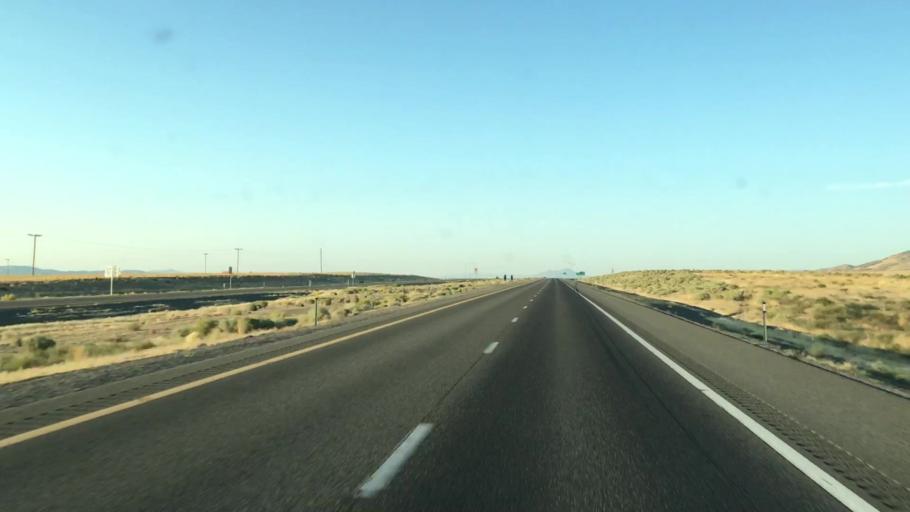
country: US
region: Nevada
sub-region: Humboldt County
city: Winnemucca
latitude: 40.7806
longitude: -118.0057
